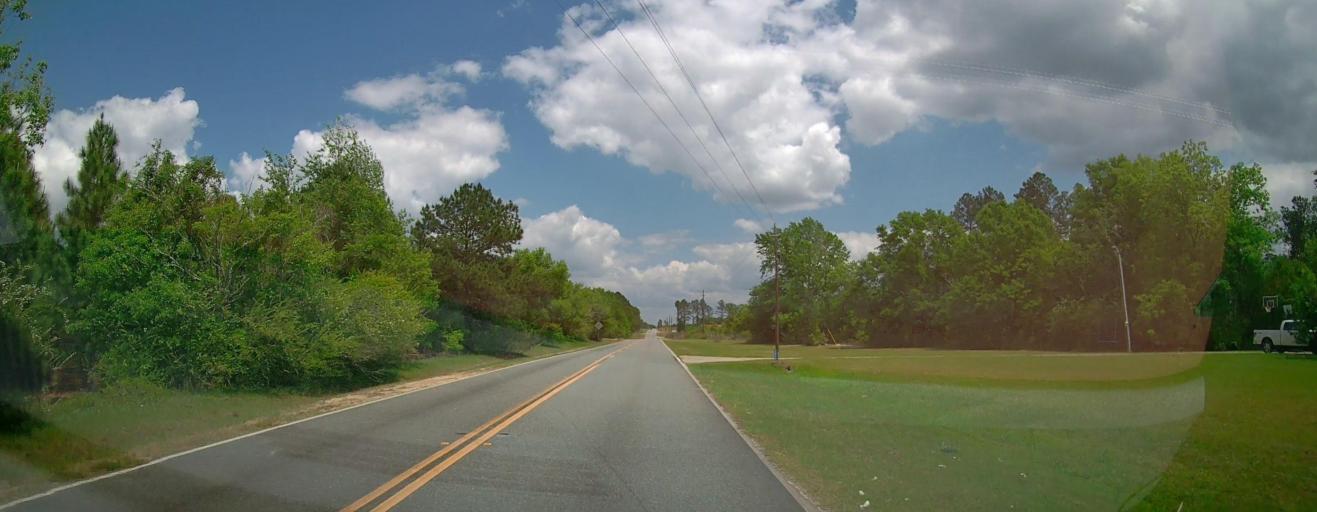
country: US
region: Georgia
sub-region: Laurens County
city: East Dublin
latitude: 32.5278
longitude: -82.7090
